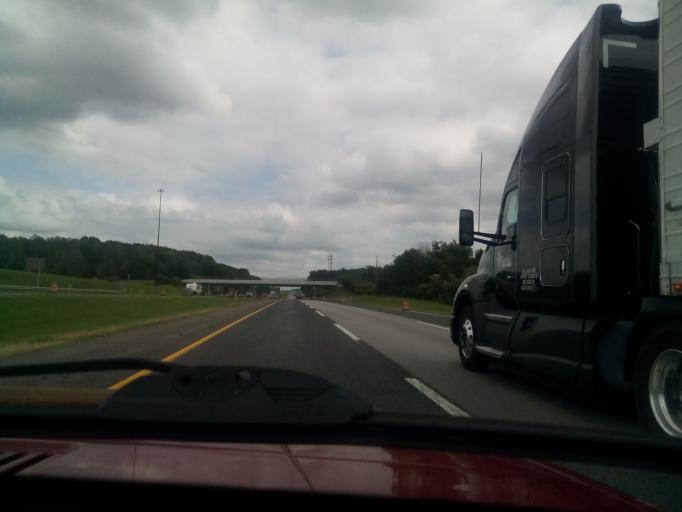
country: US
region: Indiana
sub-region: LaPorte County
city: Westville
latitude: 41.5900
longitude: -86.9004
